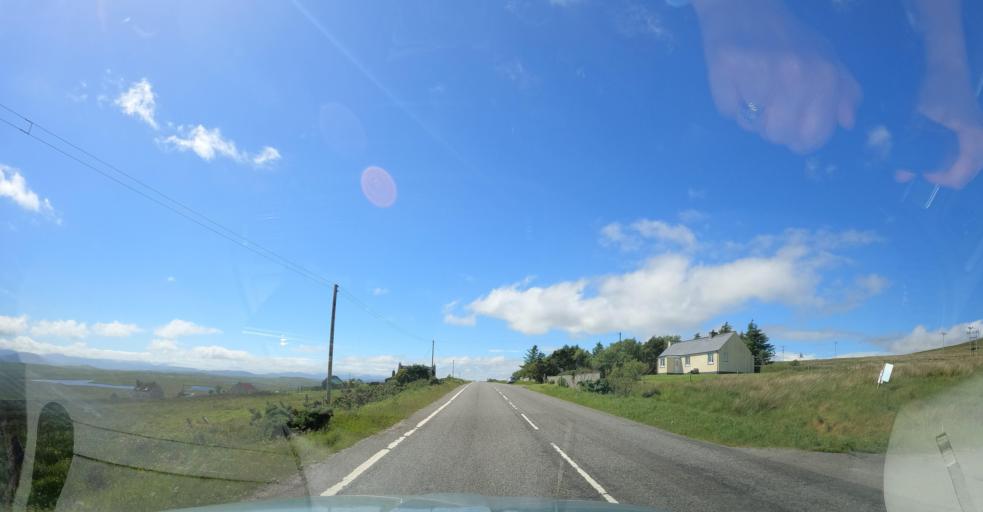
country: GB
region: Scotland
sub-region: Eilean Siar
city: Stornoway
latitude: 58.1721
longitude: -6.5839
